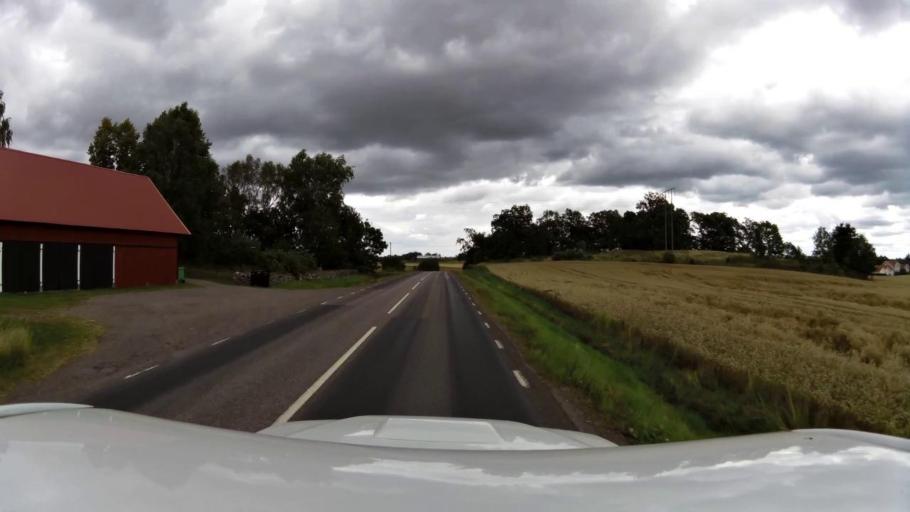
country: SE
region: OEstergoetland
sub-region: Linkopings Kommun
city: Sturefors
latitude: 58.3883
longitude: 15.7469
